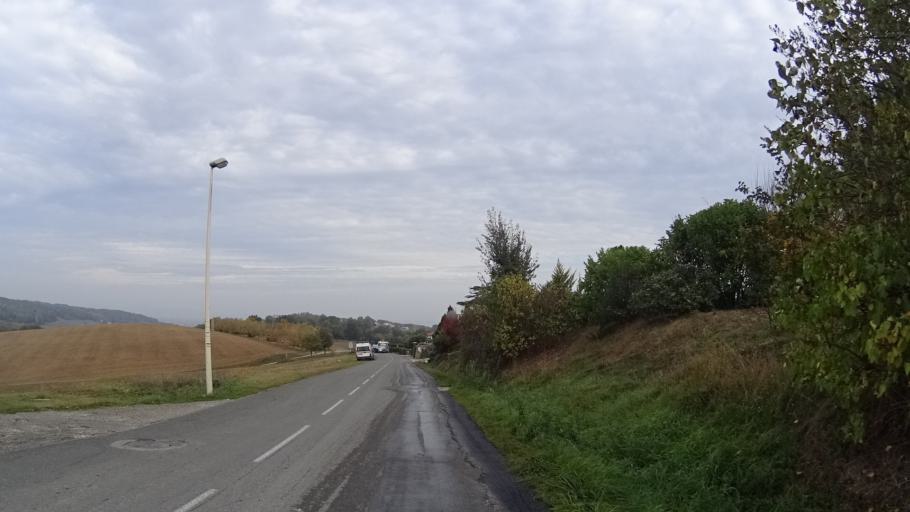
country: FR
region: Aquitaine
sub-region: Departement du Lot-et-Garonne
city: Boe
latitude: 44.1420
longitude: 0.6093
